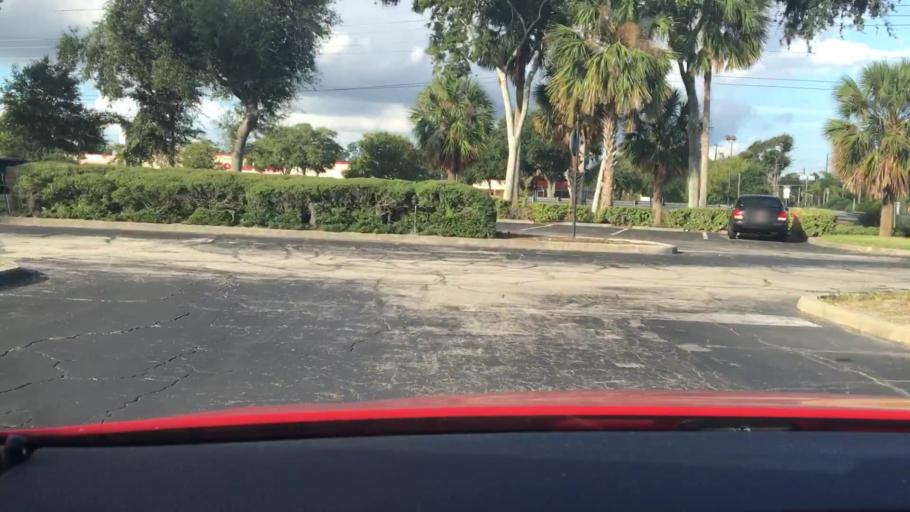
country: US
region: Florida
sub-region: Volusia County
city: South Daytona
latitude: 29.1777
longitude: -81.0280
